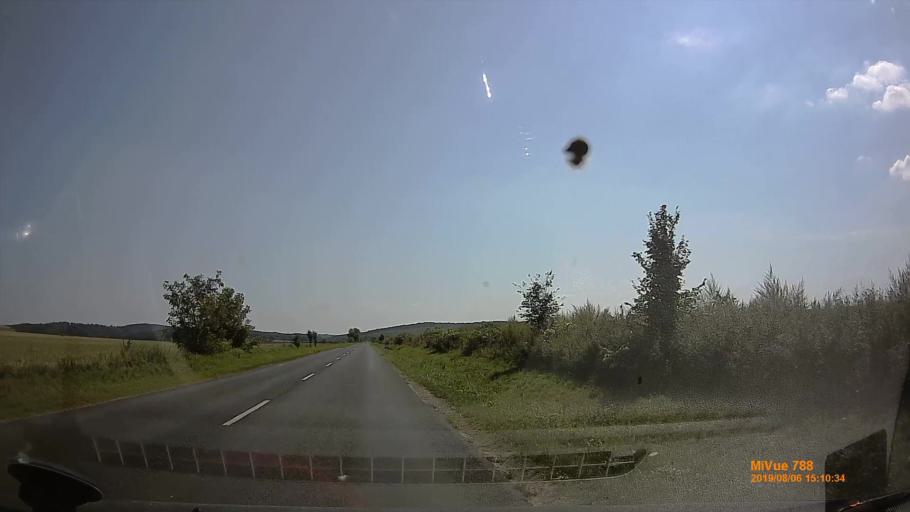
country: HU
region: Zala
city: Nagykanizsa
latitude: 46.3904
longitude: 16.9790
